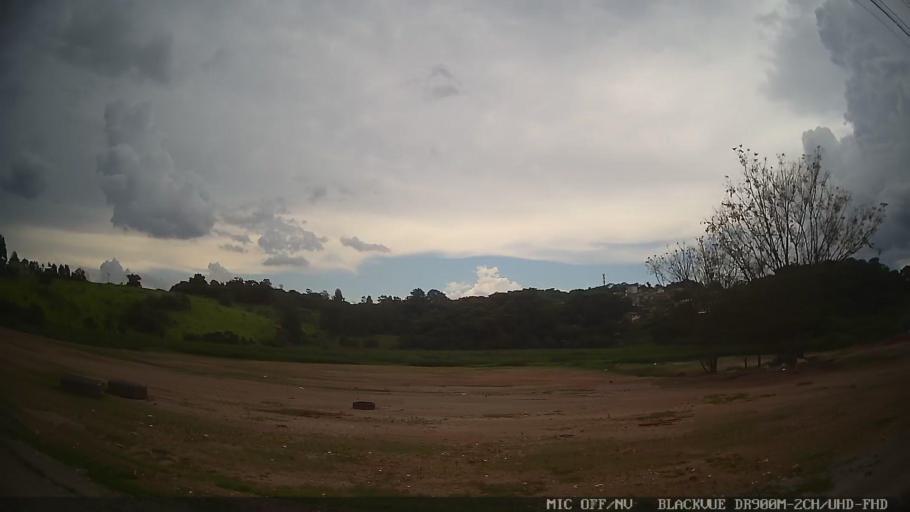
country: BR
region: Sao Paulo
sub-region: Atibaia
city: Atibaia
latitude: -23.1255
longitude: -46.5949
